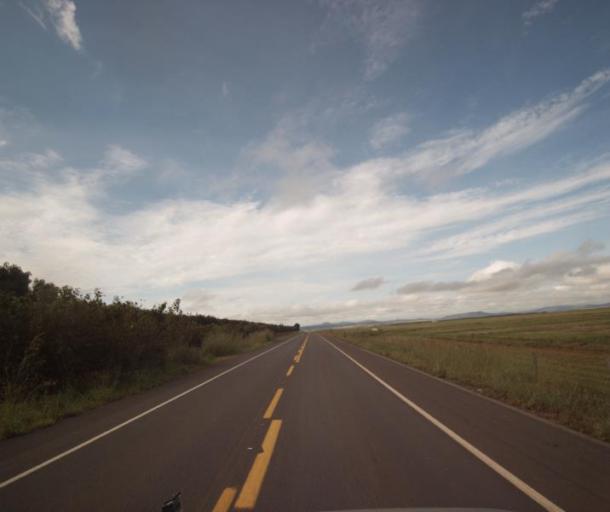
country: BR
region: Goias
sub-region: Padre Bernardo
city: Padre Bernardo
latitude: -15.3736
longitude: -48.6456
